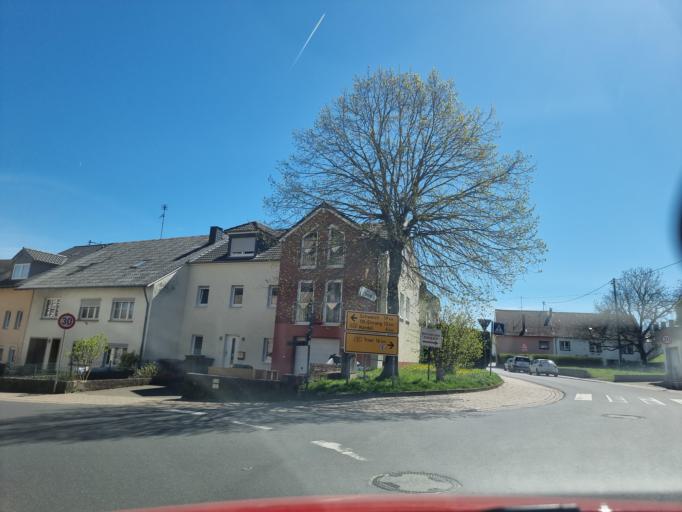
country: DE
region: Rheinland-Pfalz
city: Welschbillig
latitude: 49.8529
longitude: 6.5689
